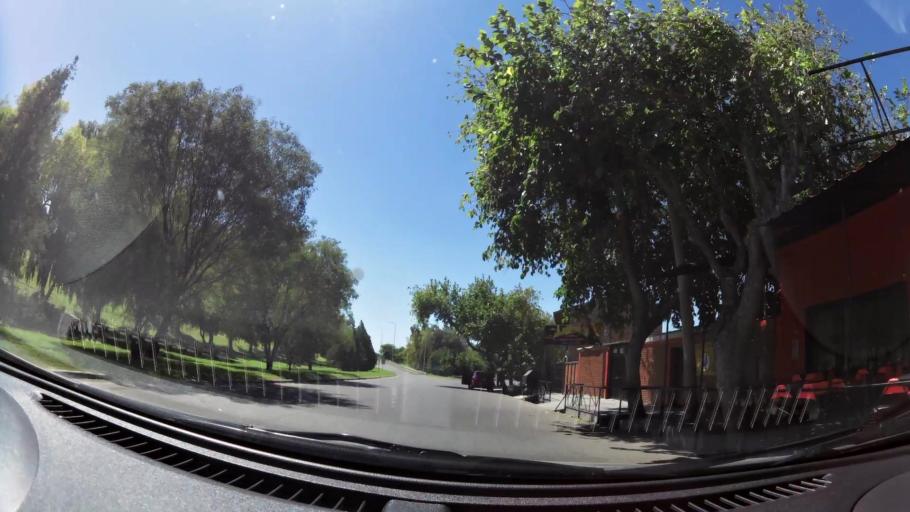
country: AR
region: San Juan
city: San Juan
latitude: -31.5209
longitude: -68.5365
